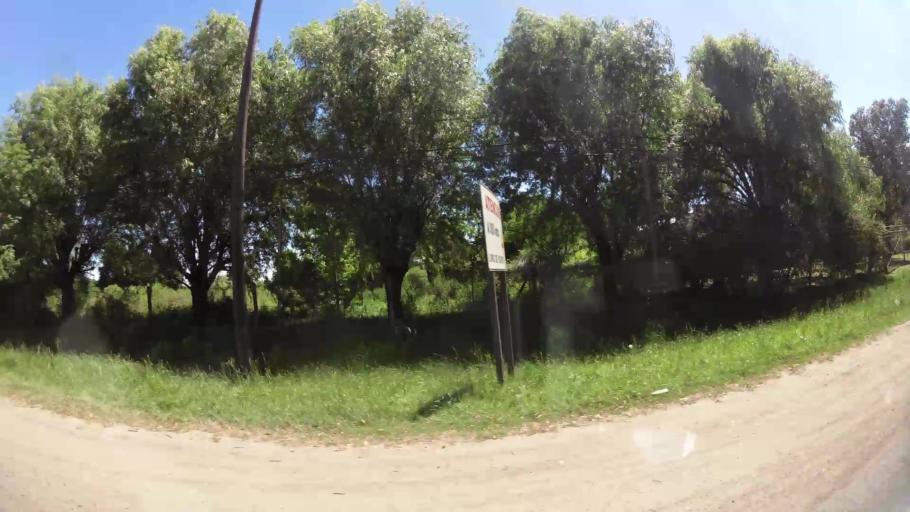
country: AR
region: Santa Fe
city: Esperanza
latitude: -31.4396
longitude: -60.9422
